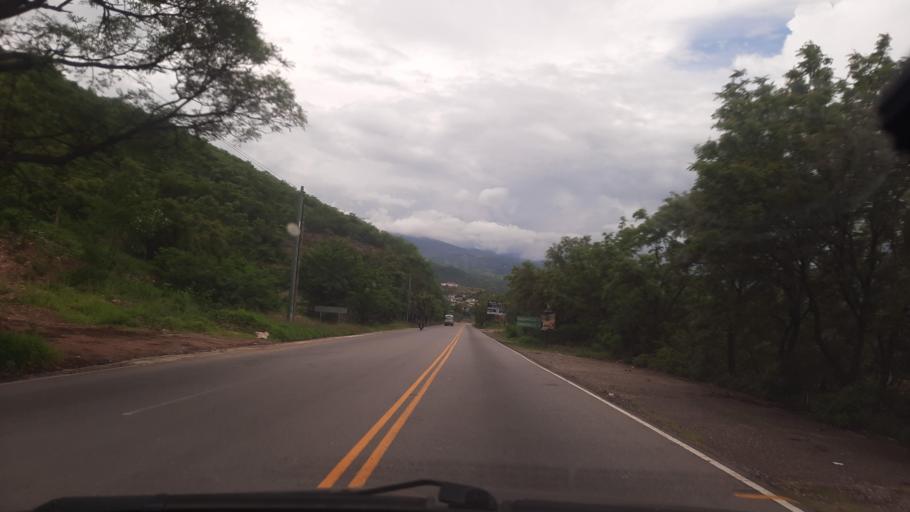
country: GT
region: Chiquimula
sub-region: Municipio de Chiquimula
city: Chiquimula
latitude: 14.8533
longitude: -89.5188
